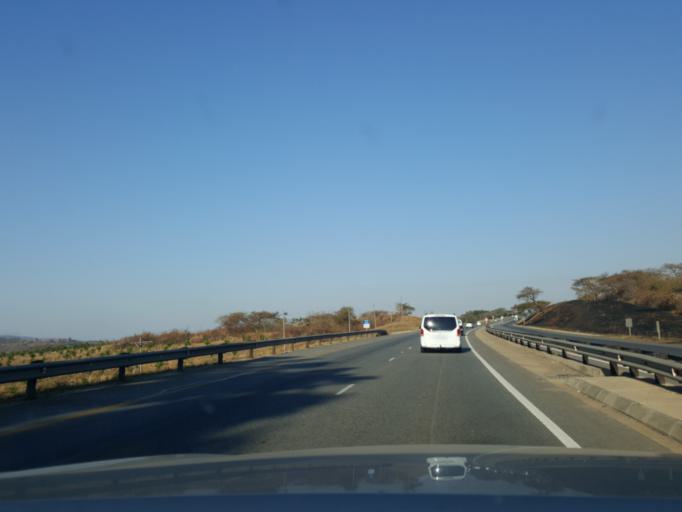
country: ZA
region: Mpumalanga
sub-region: Ehlanzeni District
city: Nelspruit
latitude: -25.4316
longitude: 30.7960
